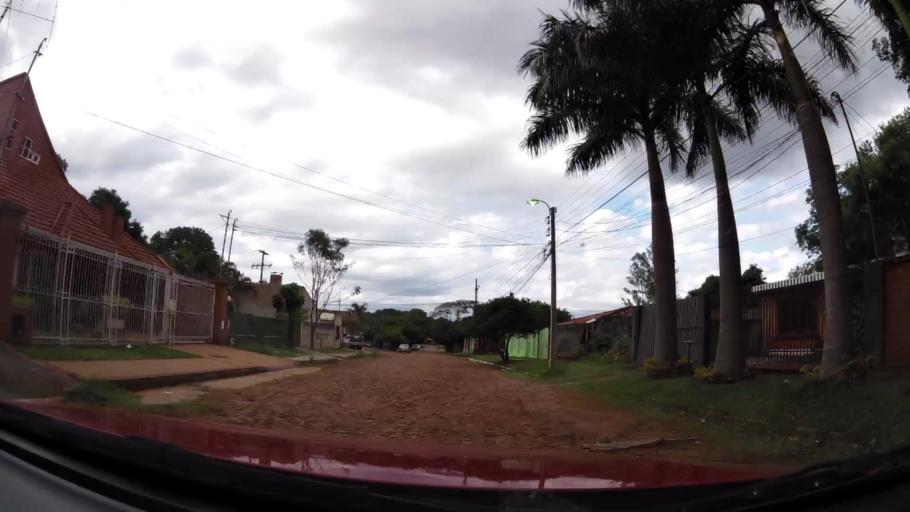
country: PY
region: Central
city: San Lorenzo
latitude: -25.2830
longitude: -57.4980
